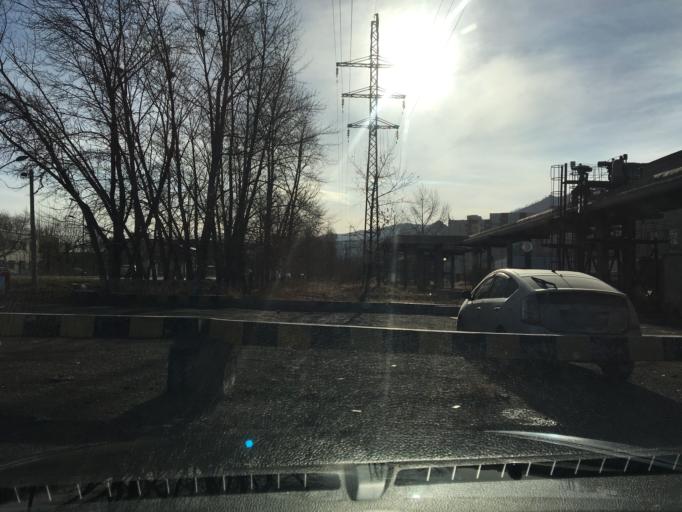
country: MN
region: Ulaanbaatar
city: Ulaanbaatar
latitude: 47.8952
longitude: 106.8732
